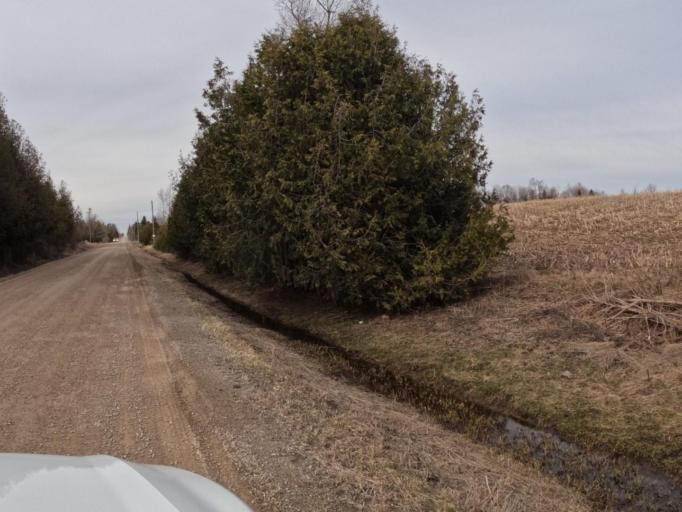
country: CA
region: Ontario
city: Shelburne
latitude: 43.9407
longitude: -80.2600
